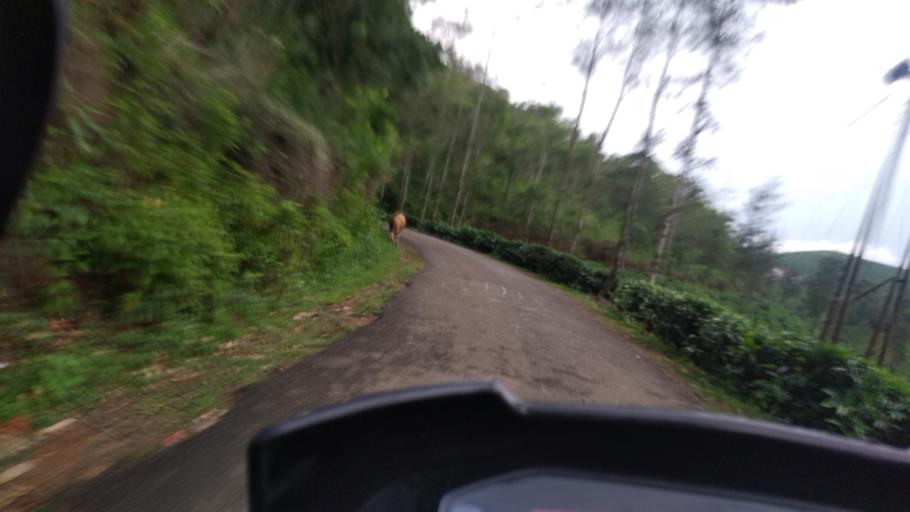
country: IN
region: Tamil Nadu
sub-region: Theni
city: Gudalur
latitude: 9.5458
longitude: 77.0519
